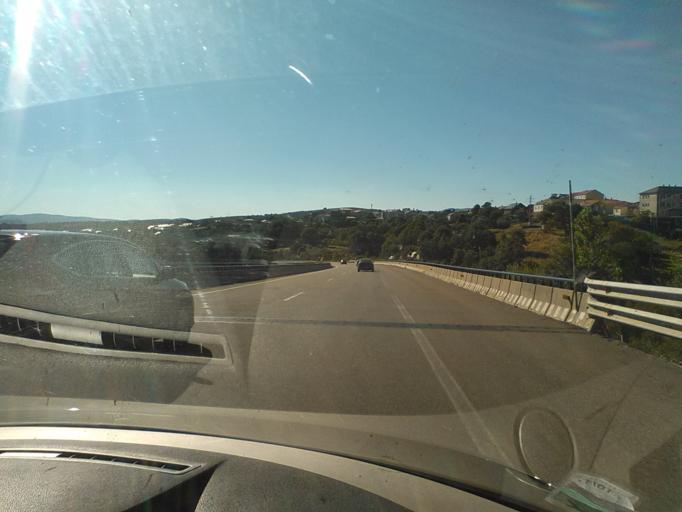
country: ES
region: Galicia
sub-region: Provincia de Ourense
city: Vilarino de Conso
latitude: 42.0580
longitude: -7.1313
